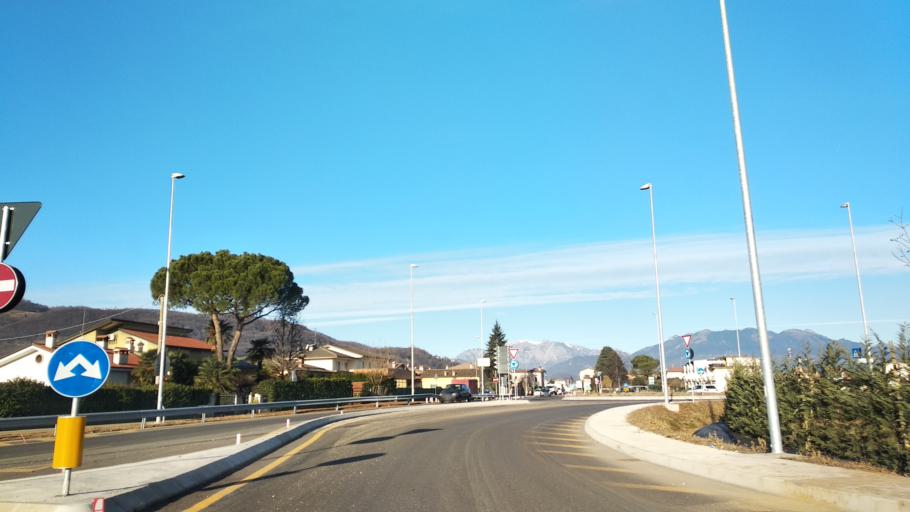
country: IT
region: Veneto
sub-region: Provincia di Vicenza
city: Isola Vicentina
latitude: 45.6373
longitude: 11.4360
